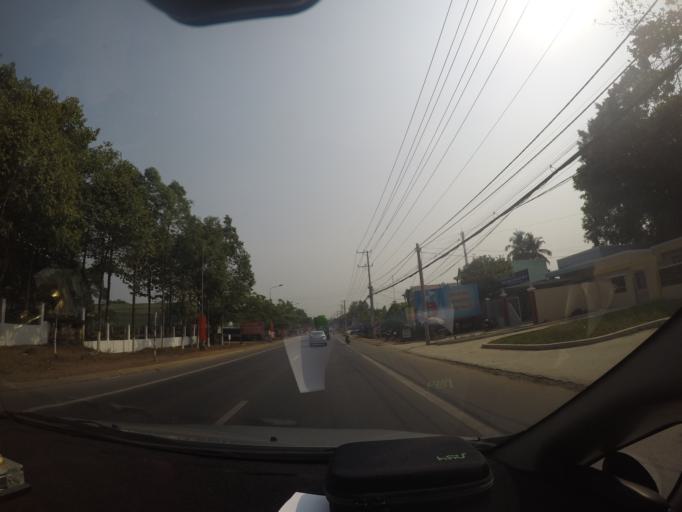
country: VN
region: Dong Nai
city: Tan Phu
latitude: 11.1914
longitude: 107.3490
